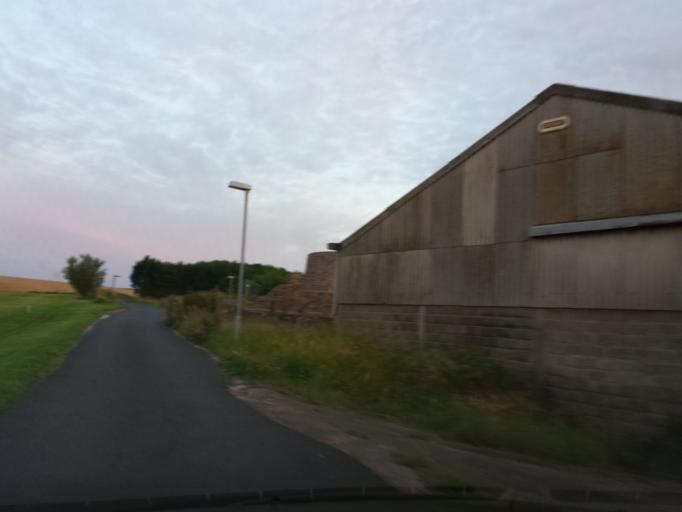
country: GB
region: Scotland
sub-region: The Scottish Borders
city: Eyemouth
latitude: 55.8671
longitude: -2.0851
